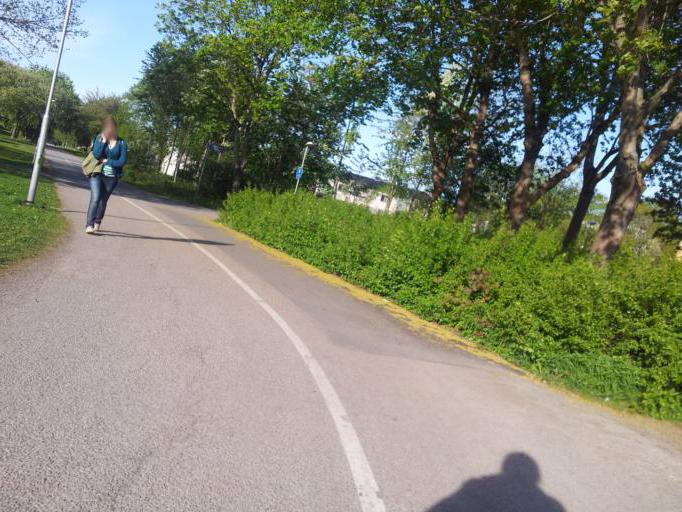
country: SE
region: Uppsala
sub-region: Uppsala Kommun
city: Uppsala
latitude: 59.8694
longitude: 17.6409
